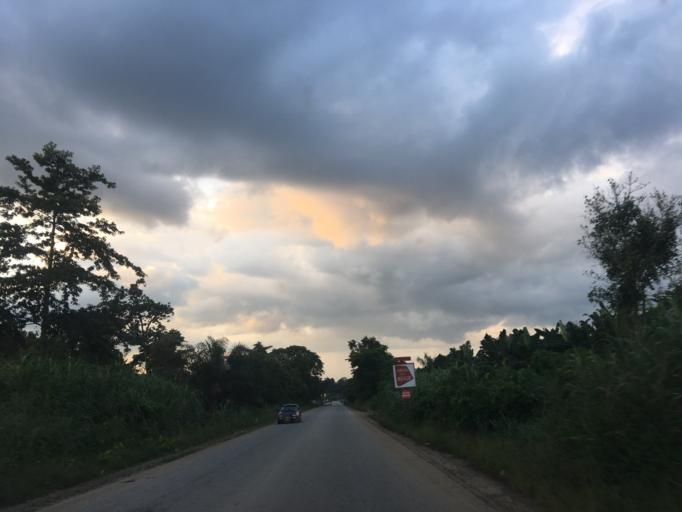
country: GH
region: Western
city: Bibiani
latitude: 6.7460
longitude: -2.5040
